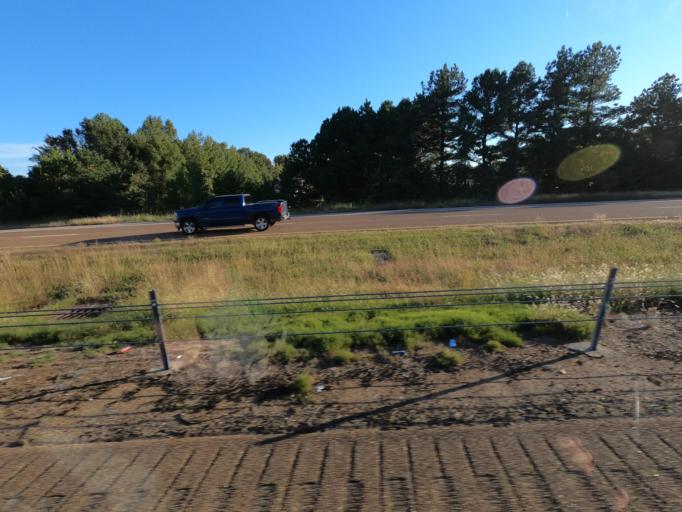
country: US
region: Tennessee
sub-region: Shelby County
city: Lakeland
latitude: 35.3077
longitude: -89.7973
